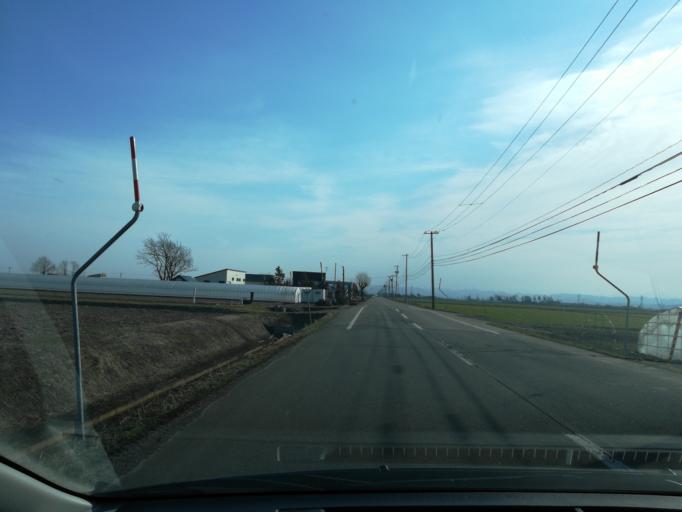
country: JP
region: Hokkaido
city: Iwamizawa
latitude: 43.1667
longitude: 141.6608
